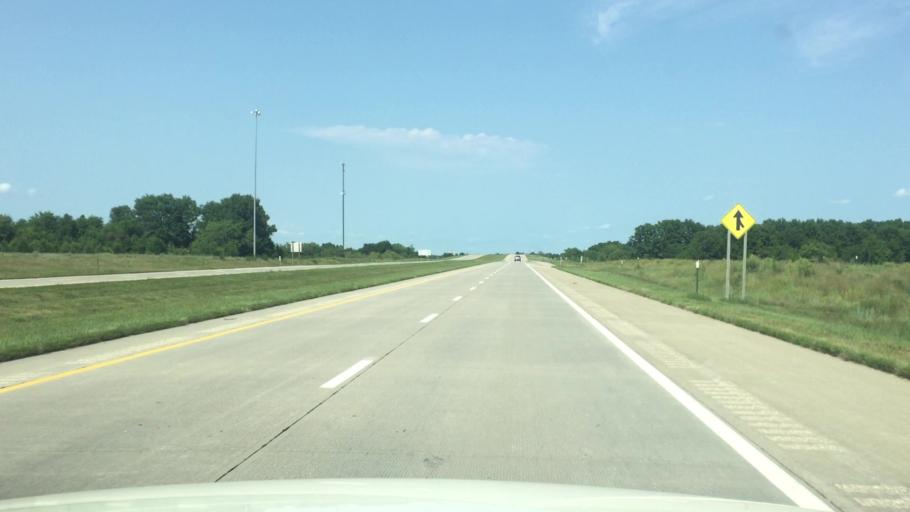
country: US
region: Kansas
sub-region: Linn County
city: Pleasanton
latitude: 38.1474
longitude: -94.7054
